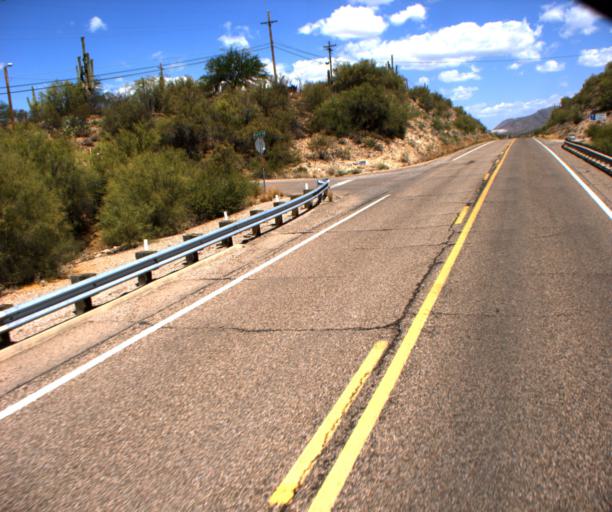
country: US
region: Arizona
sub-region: Pinal County
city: Kearny
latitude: 33.0823
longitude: -110.9257
